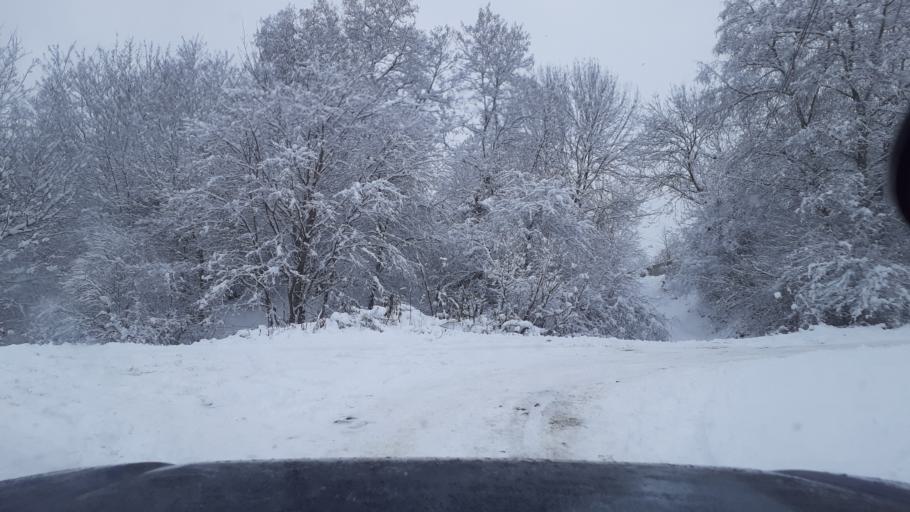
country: RU
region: Adygeya
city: Kamennomostskiy
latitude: 44.2362
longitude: 40.2042
